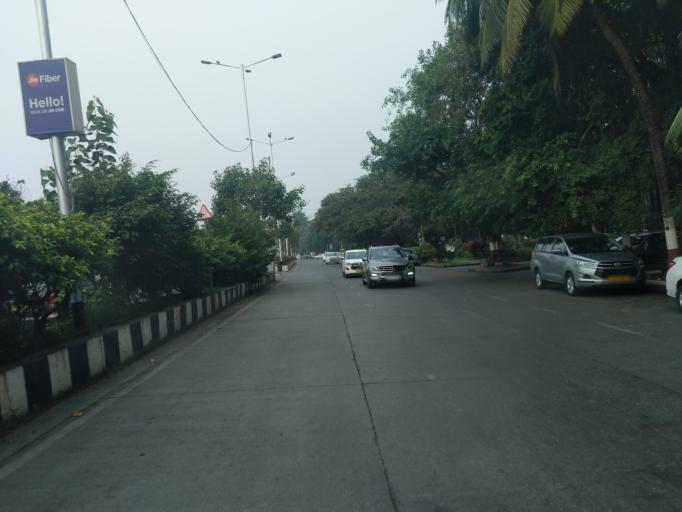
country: IN
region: Maharashtra
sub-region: Raigarh
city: Uran
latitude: 18.9283
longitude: 72.8211
